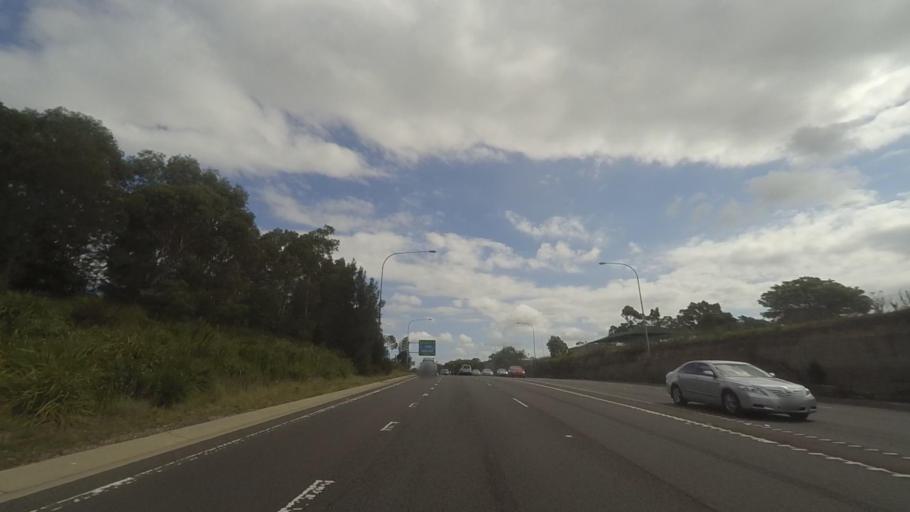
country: AU
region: New South Wales
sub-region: Sutherland Shire
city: Menai
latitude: -34.0101
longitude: 151.0109
